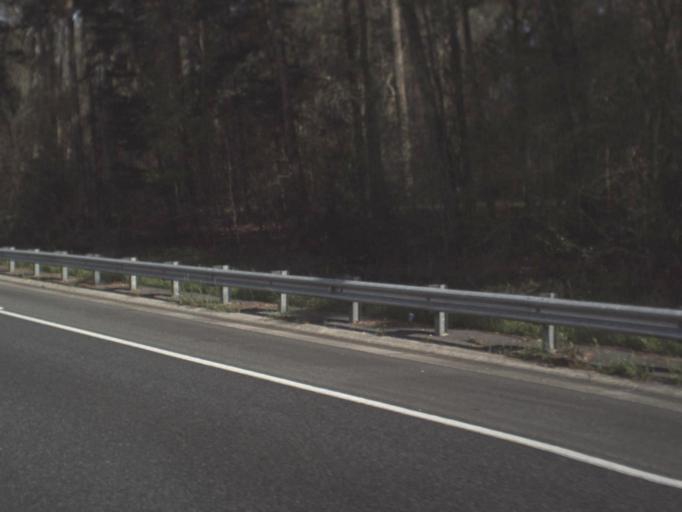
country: US
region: Florida
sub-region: Leon County
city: Tallahassee
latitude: 30.4990
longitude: -84.2638
